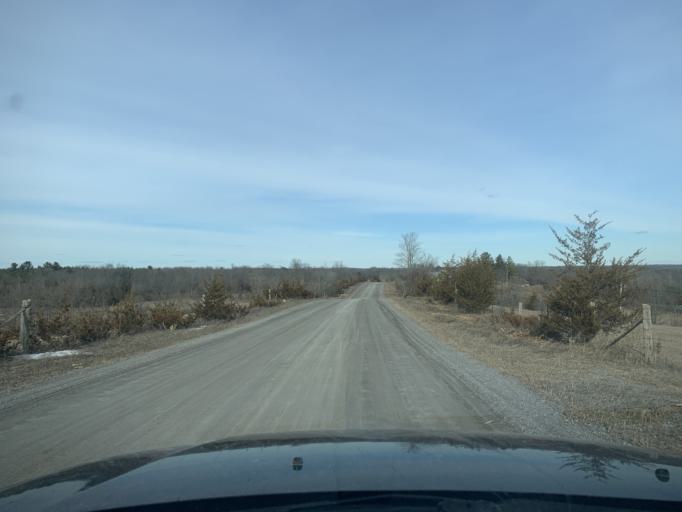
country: CA
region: Ontario
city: Deseronto
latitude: 44.4018
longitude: -77.1309
